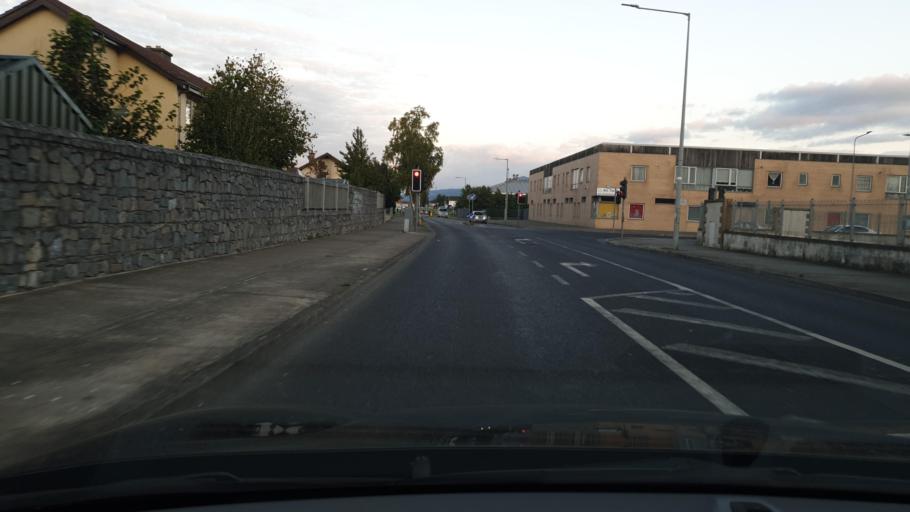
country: IE
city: Jobstown
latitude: 53.2836
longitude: -6.4023
